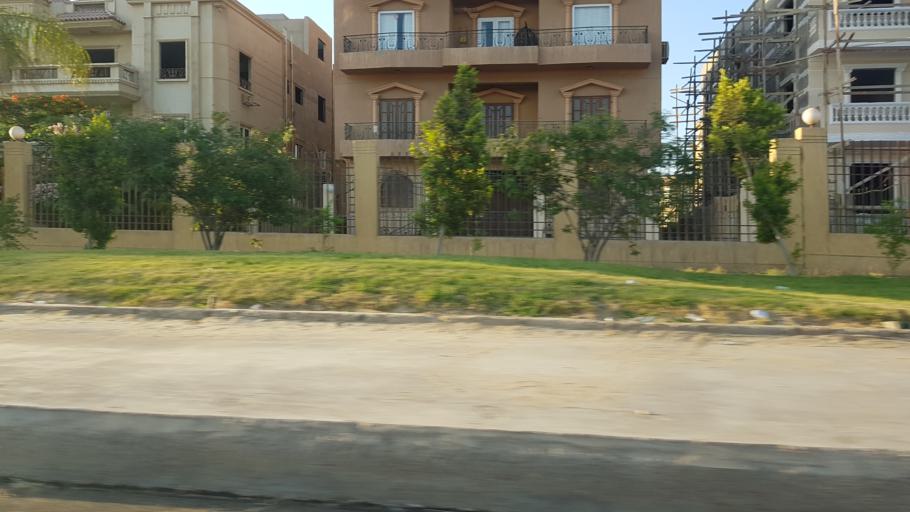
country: EG
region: Muhafazat al Qalyubiyah
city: Al Khankah
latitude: 30.0613
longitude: 31.4425
